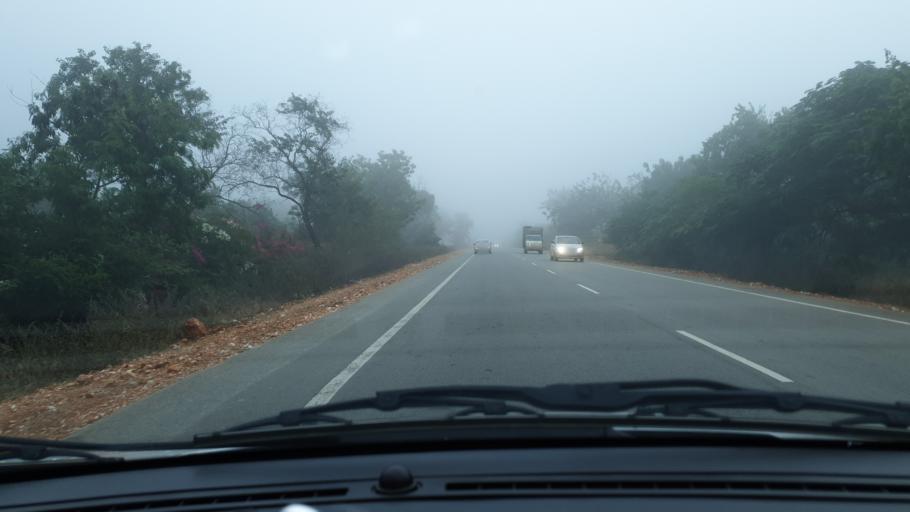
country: IN
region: Telangana
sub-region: Mahbubnagar
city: Nagar Karnul
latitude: 16.6414
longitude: 78.5916
